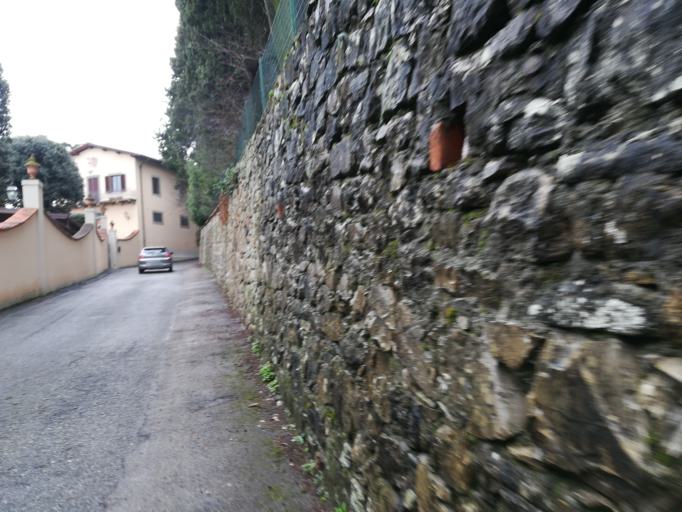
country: IT
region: Tuscany
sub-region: Provincia di Prato
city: Comeana
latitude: 43.7969
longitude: 11.0503
